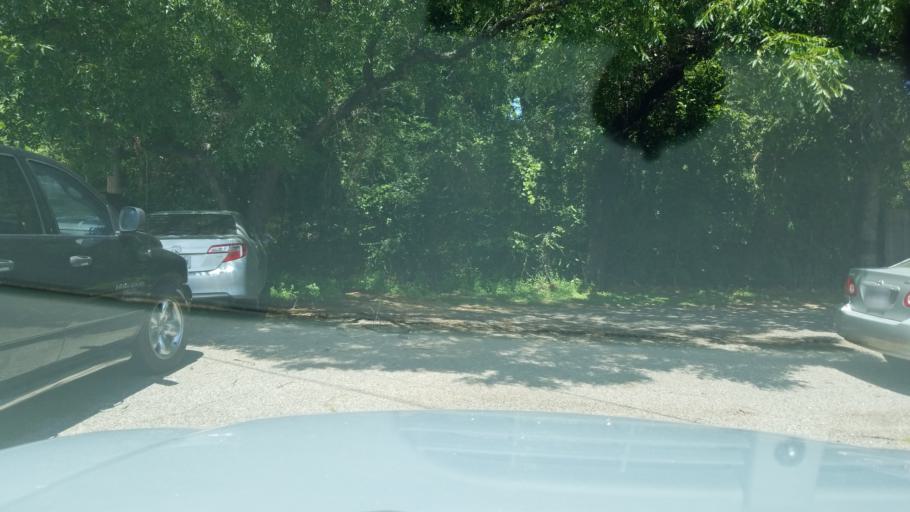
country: US
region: Texas
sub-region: Dallas County
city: Irving
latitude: 32.8056
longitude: -96.9243
